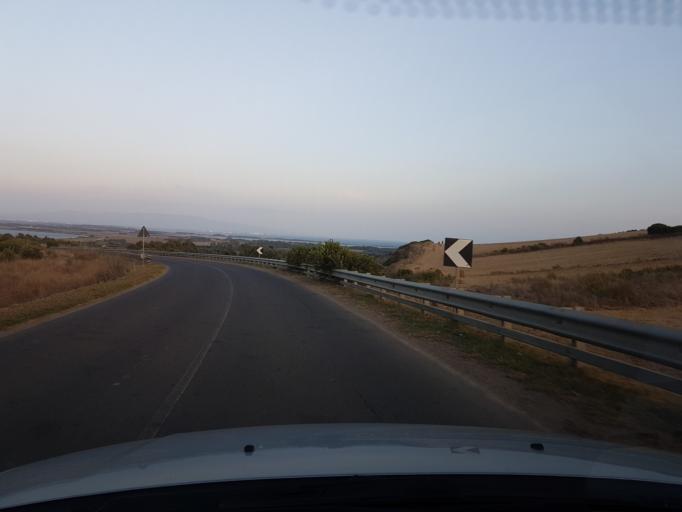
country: IT
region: Sardinia
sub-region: Provincia di Oristano
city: Cabras
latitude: 39.9319
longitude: 8.4492
